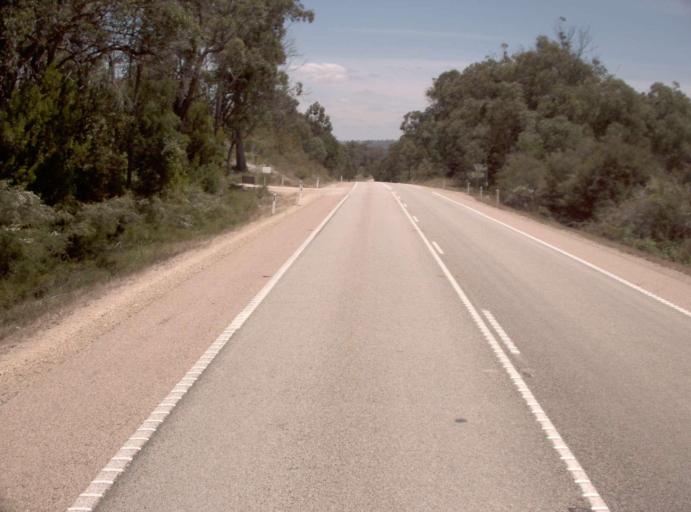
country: AU
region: Victoria
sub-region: East Gippsland
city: Bairnsdale
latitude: -37.7482
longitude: 147.7539
